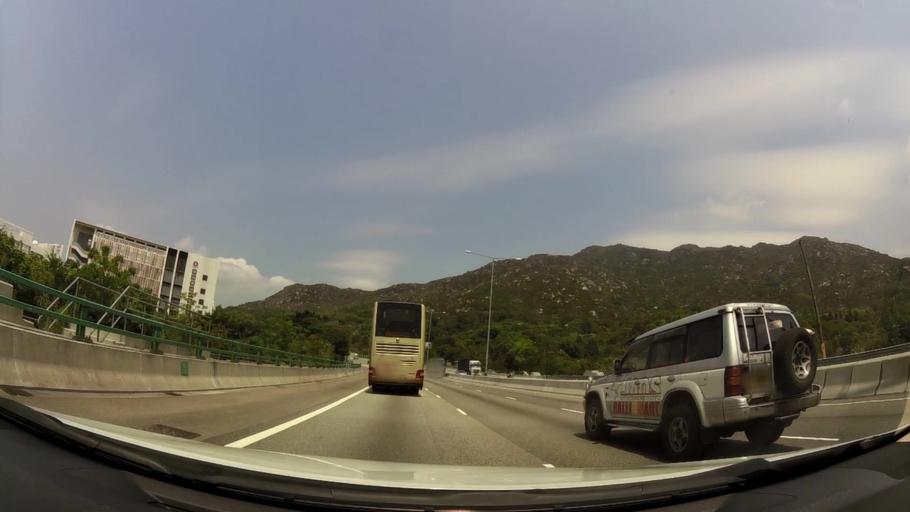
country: HK
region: Tuen Mun
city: Tuen Mun
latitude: 22.3740
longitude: 113.9972
